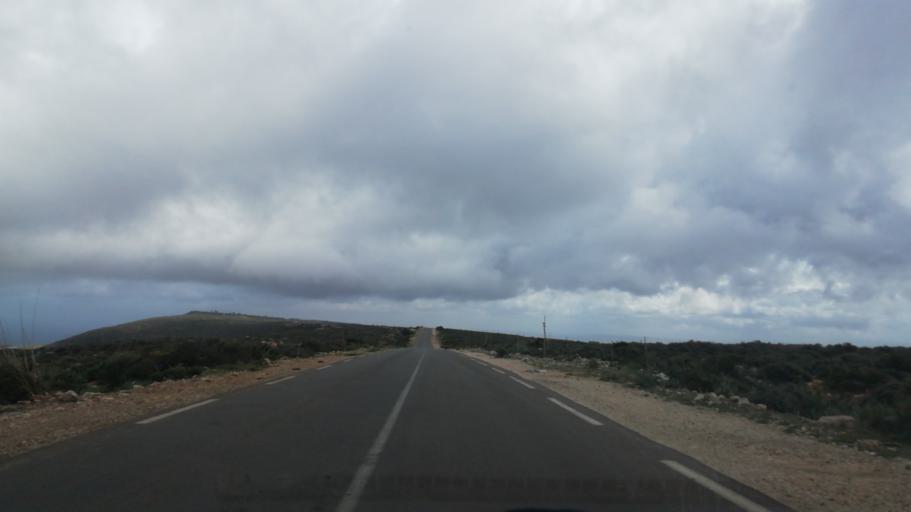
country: DZ
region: Oran
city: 'Ain el Turk
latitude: 35.6994
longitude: -0.7593
